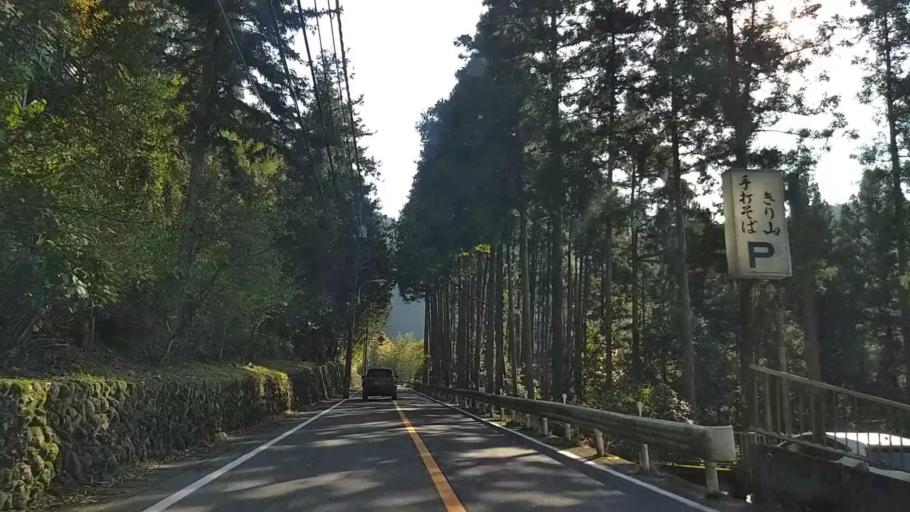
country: JP
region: Tokyo
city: Ome
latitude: 35.8035
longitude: 139.1768
